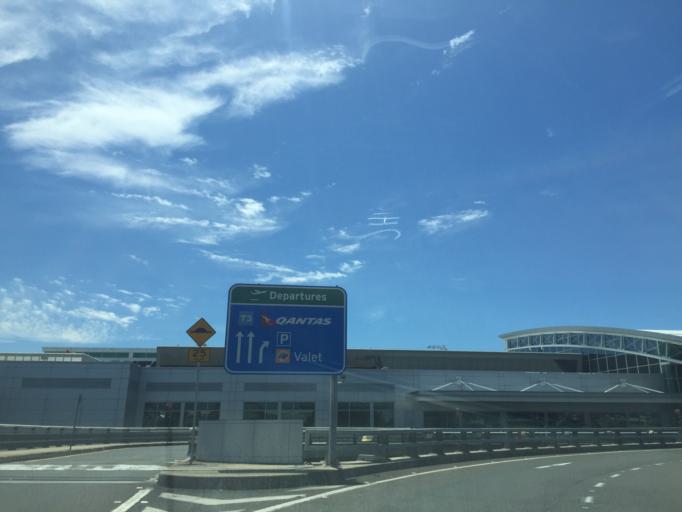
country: AU
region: New South Wales
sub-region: Botany Bay
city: Mascot
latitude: -33.9330
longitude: 151.1782
